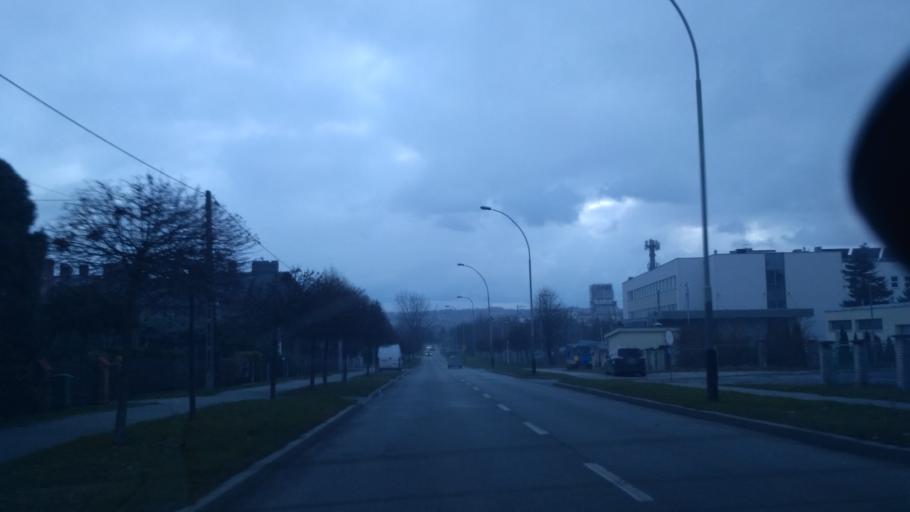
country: PL
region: Subcarpathian Voivodeship
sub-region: Rzeszow
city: Rzeszow
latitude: 50.0364
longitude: 22.0404
